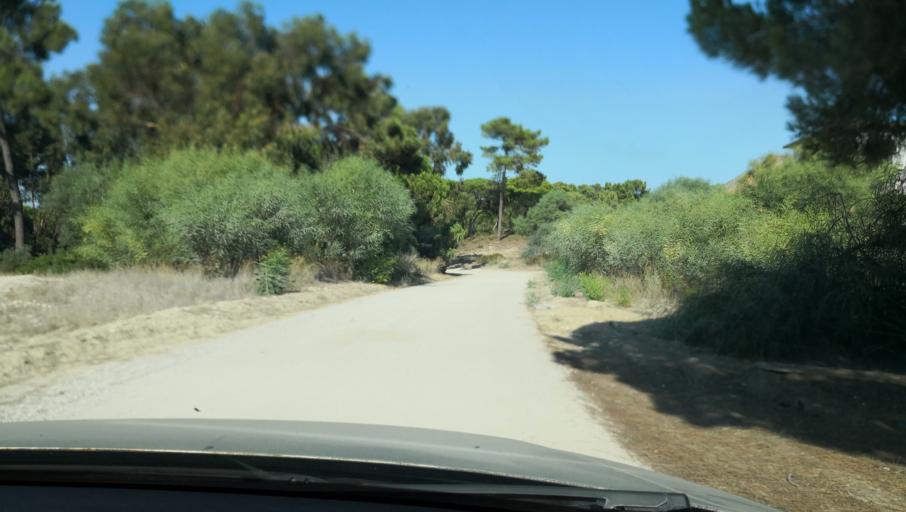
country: PT
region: Setubal
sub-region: Setubal
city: Setubal
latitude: 38.4673
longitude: -8.8738
